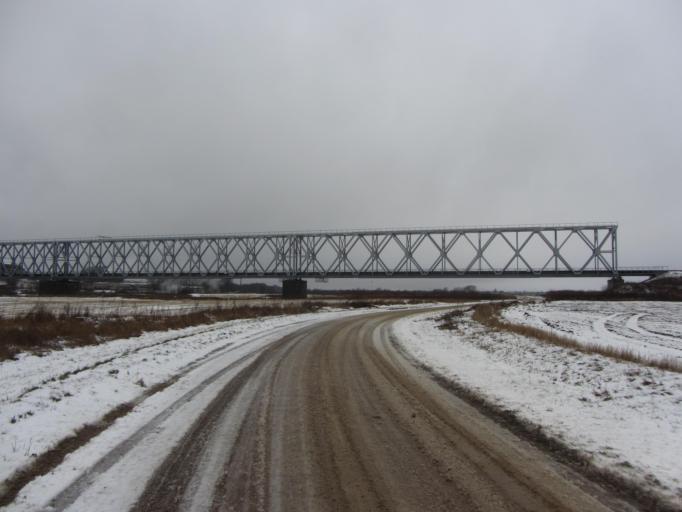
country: RU
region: Kaliningrad
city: Sovetsk
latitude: 55.0925
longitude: 21.8916
